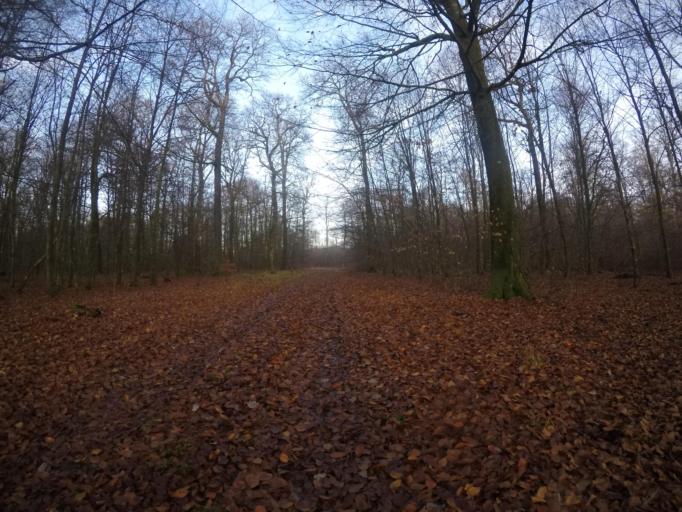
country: BE
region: Wallonia
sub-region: Province du Luxembourg
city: Habay-la-Vieille
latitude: 49.7500
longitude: 5.6725
